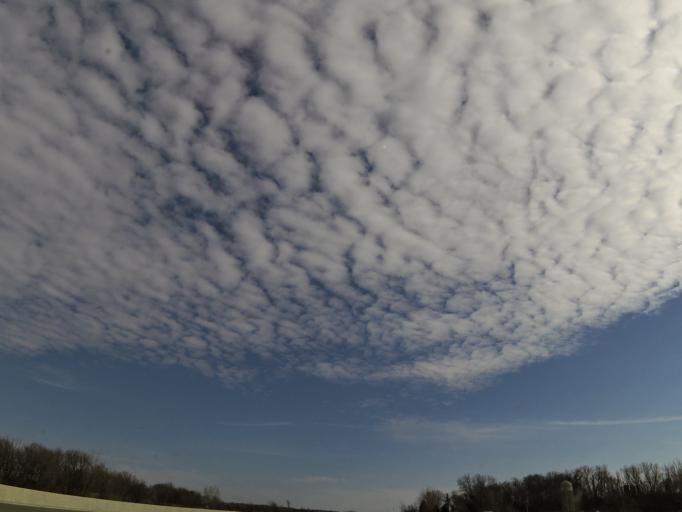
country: US
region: Minnesota
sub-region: Steele County
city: Medford
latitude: 44.2098
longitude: -93.2652
